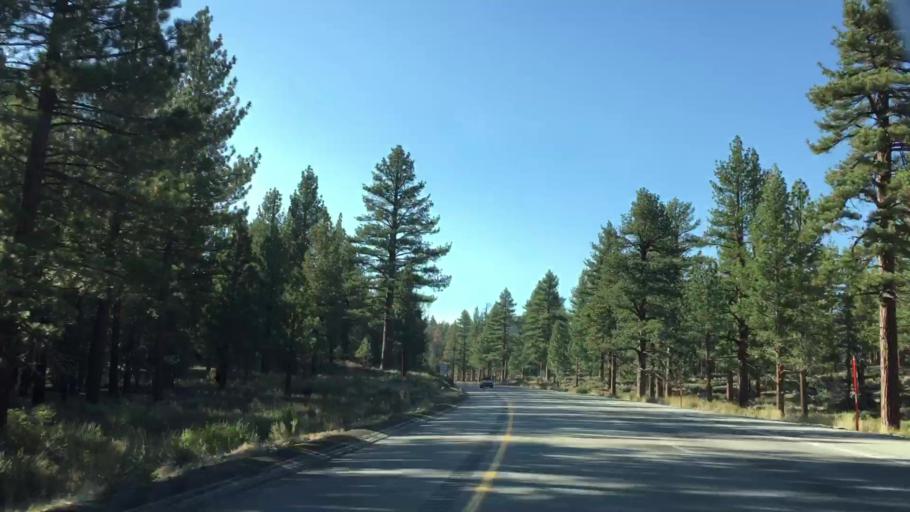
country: US
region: California
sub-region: Mono County
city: Mammoth Lakes
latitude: 37.6615
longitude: -118.9284
